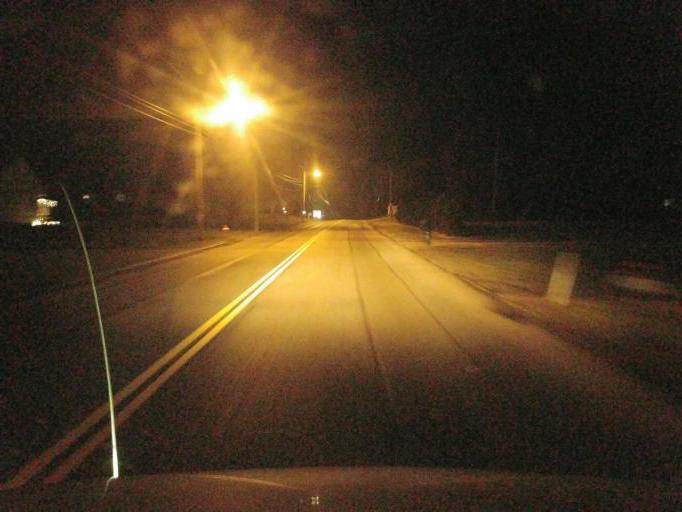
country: US
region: Ohio
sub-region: Stark County
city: Beach City
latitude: 40.6576
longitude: -81.6357
